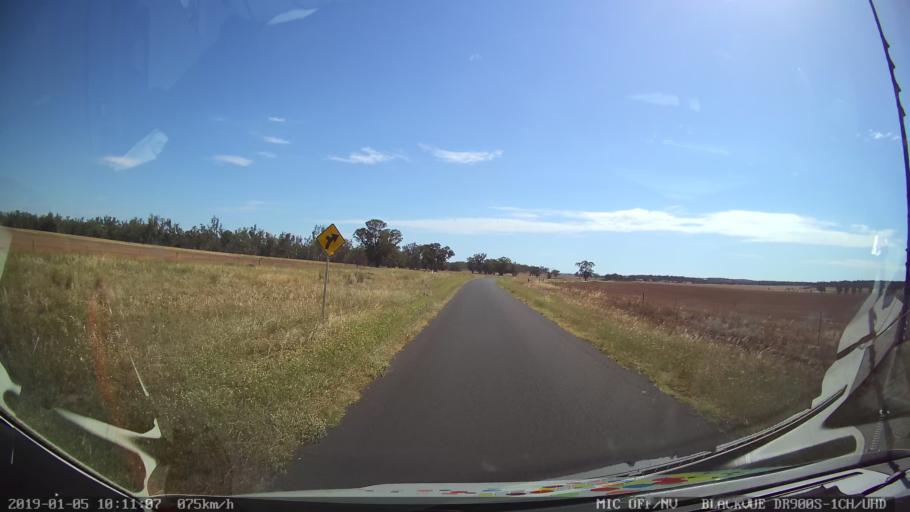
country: AU
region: New South Wales
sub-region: Gilgandra
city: Gilgandra
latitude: -31.6156
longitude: 148.8981
